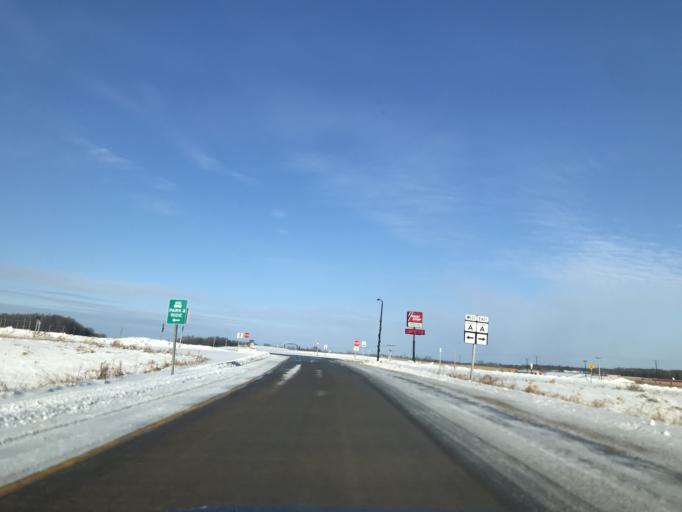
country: US
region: Wisconsin
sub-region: Oconto County
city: Oconto Falls
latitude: 44.9499
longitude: -88.0356
